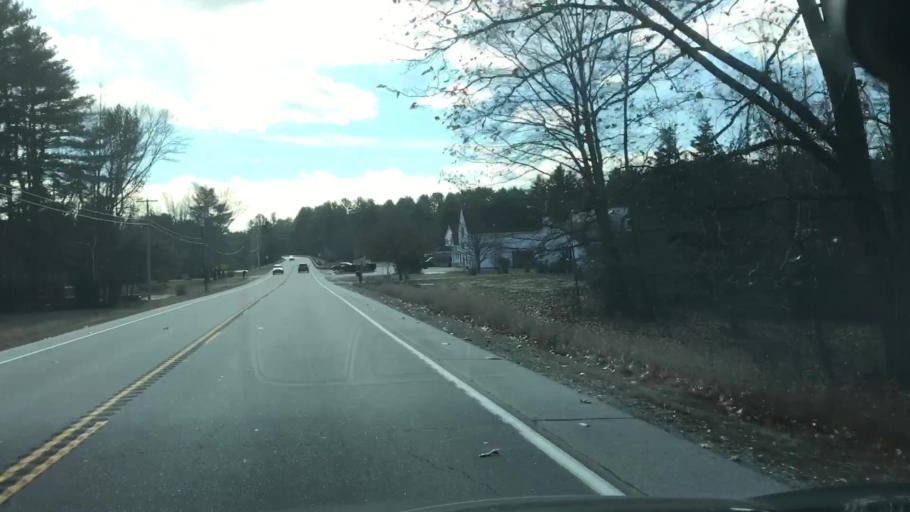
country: US
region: New Hampshire
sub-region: Merrimack County
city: Chichester
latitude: 43.2559
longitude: -71.3730
